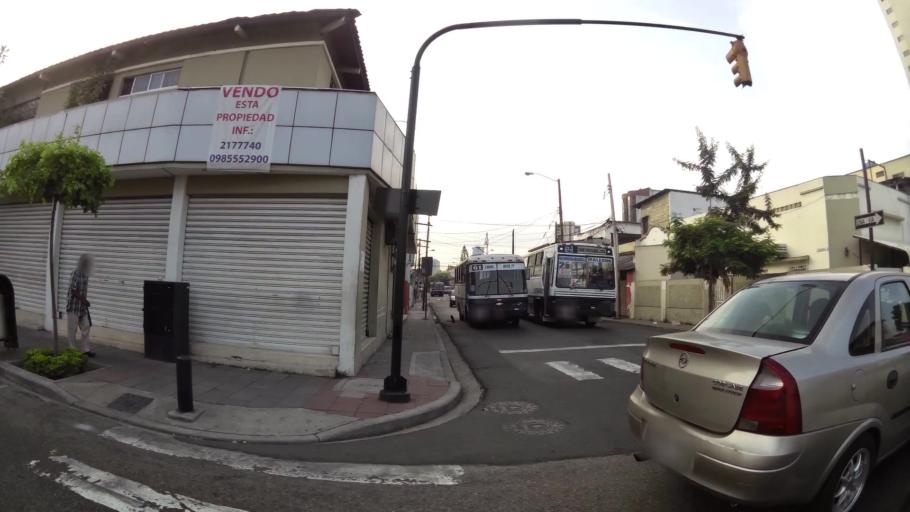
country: EC
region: Guayas
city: Guayaquil
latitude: -2.1861
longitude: -79.8934
